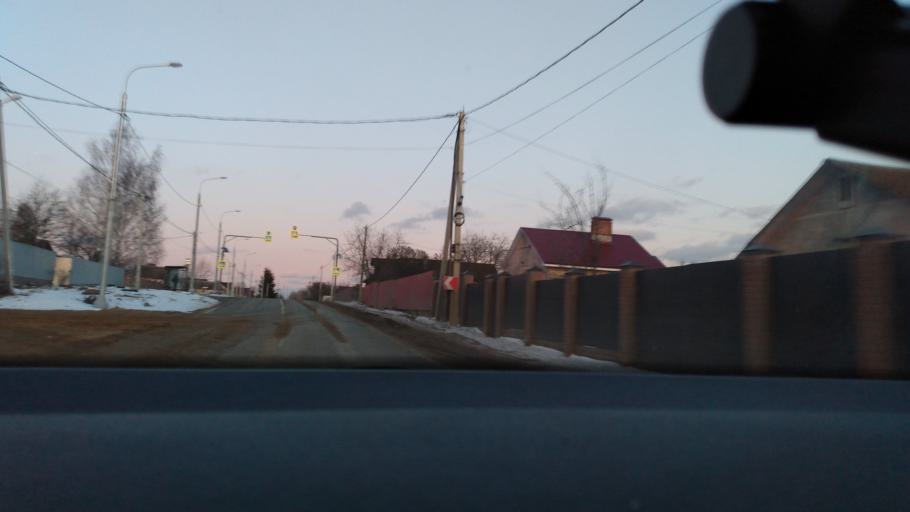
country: RU
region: Moskovskaya
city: Krasnaya Poyma
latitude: 55.1063
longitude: 39.0095
